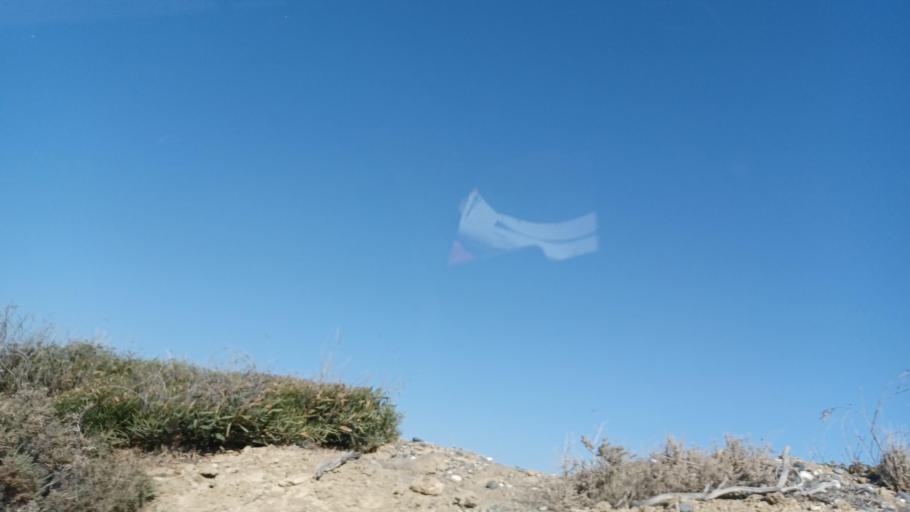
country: CY
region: Larnaka
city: Kolossi
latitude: 34.6033
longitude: 32.9319
